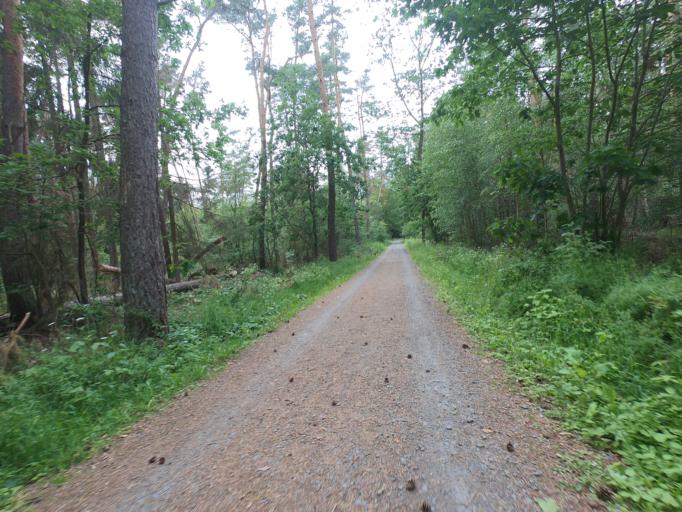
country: DE
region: Hesse
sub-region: Regierungsbezirk Darmstadt
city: Offenbach
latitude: 50.0619
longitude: 8.7596
